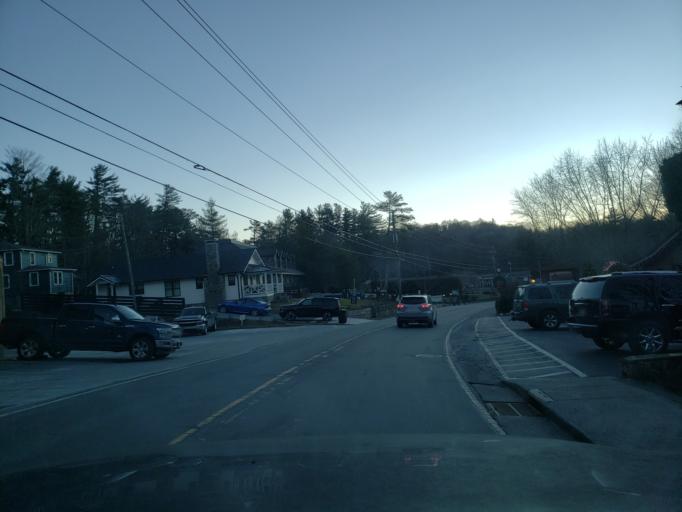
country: US
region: North Carolina
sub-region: Watauga County
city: Blowing Rock
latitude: 36.1354
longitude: -81.6774
